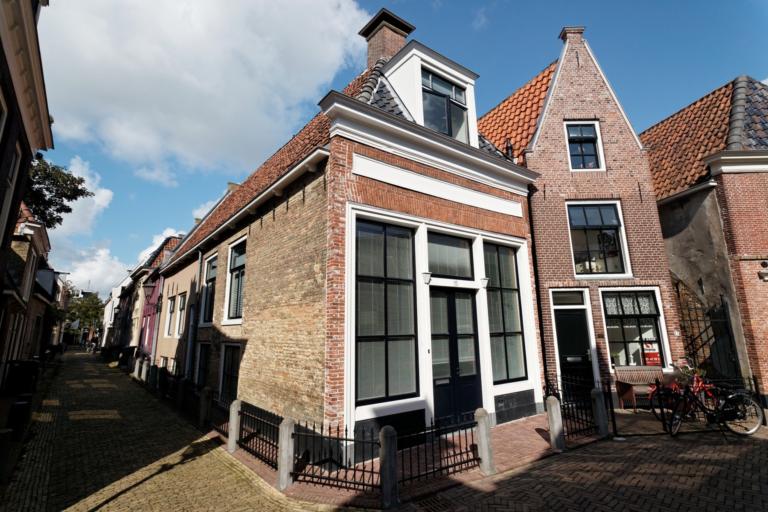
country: NL
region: Friesland
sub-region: Gemeente Harlingen
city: Harlingen
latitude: 53.1738
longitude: 5.4205
